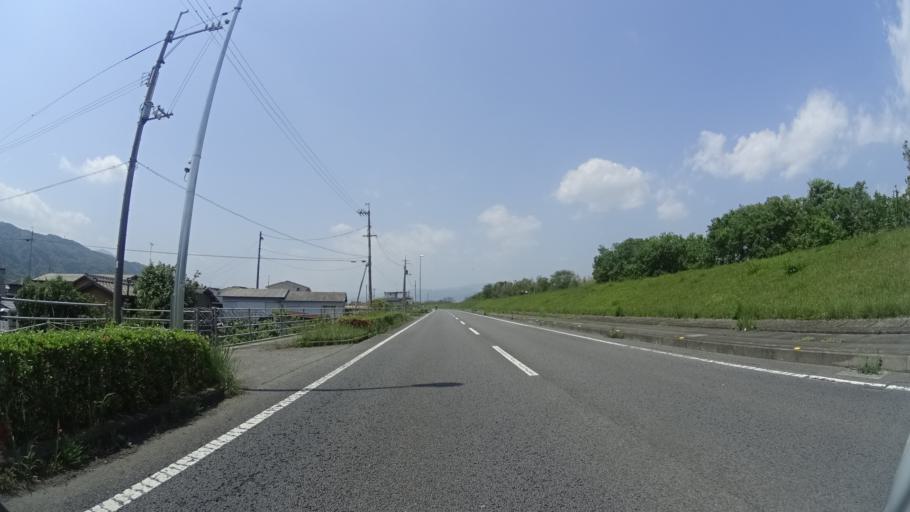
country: JP
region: Tokushima
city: Kamojimacho-jogejima
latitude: 34.0617
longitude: 134.2933
